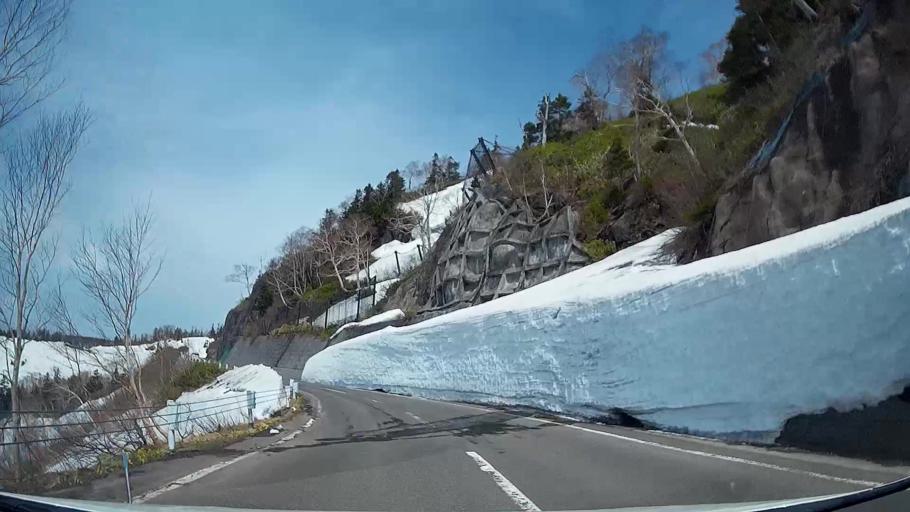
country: JP
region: Akita
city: Hanawa
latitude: 39.9502
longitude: 140.8957
